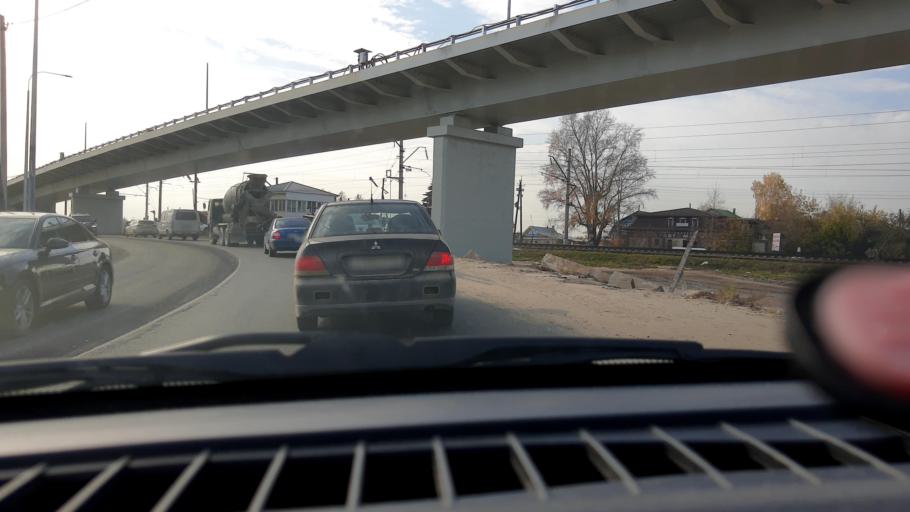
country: RU
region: Nizjnij Novgorod
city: Neklyudovo
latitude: 56.3999
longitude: 43.9827
